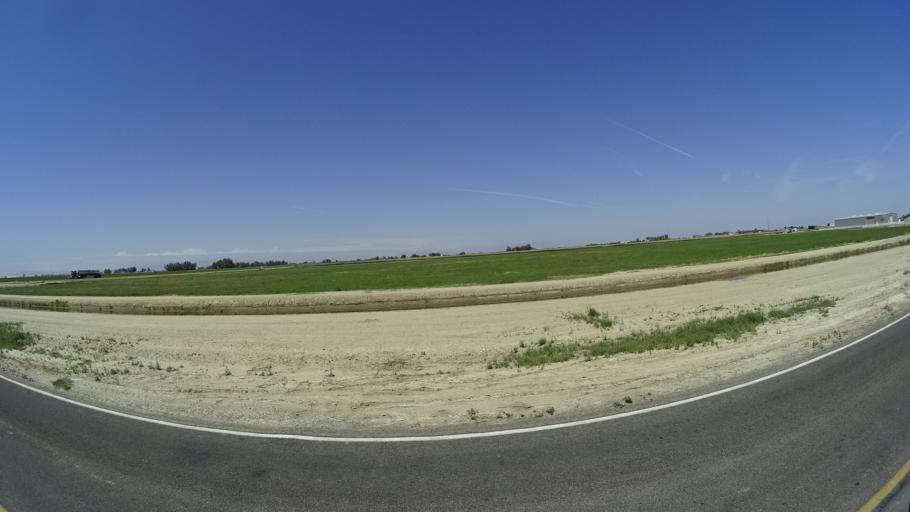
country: US
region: California
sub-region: Kings County
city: Stratford
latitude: 36.2122
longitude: -119.7625
